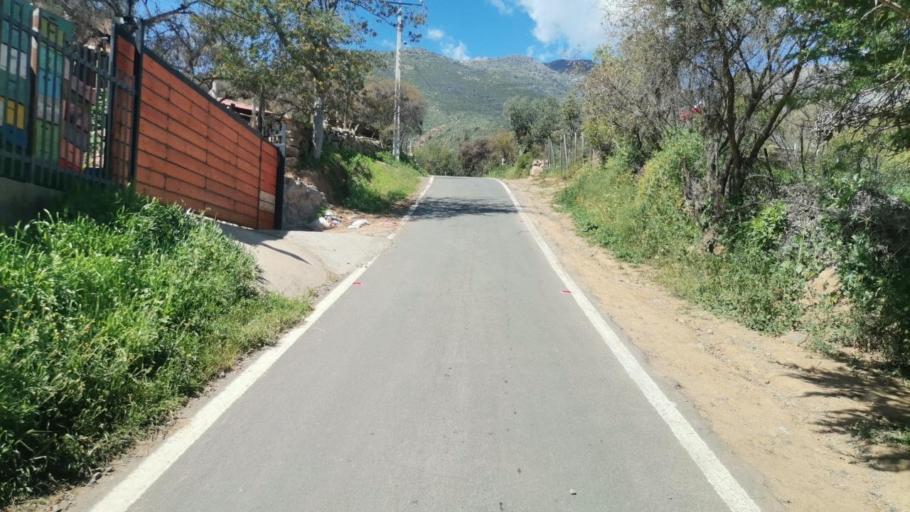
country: CL
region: Santiago Metropolitan
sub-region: Provincia de Chacabuco
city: Lampa
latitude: -33.1946
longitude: -71.0937
